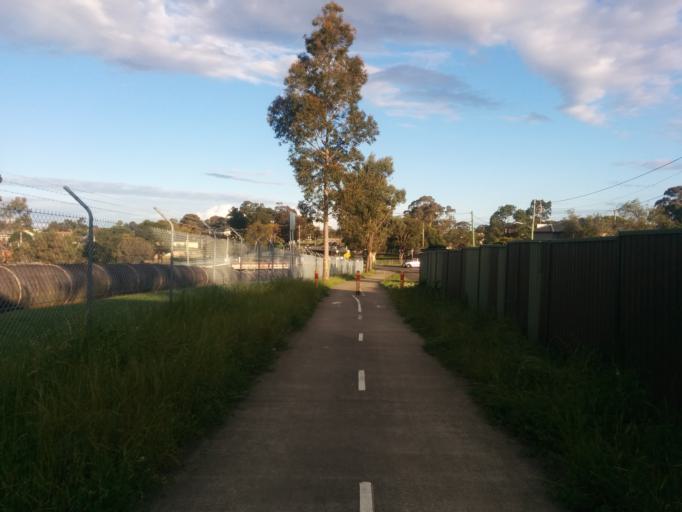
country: AU
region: New South Wales
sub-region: Holroyd
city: Guildford West
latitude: -33.8505
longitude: 150.9742
